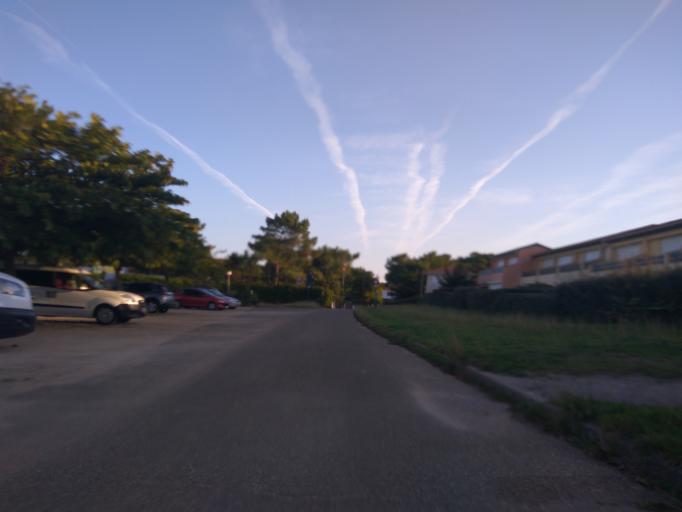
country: FR
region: Aquitaine
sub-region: Departement des Landes
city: Capbreton
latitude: 43.6469
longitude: -1.4425
